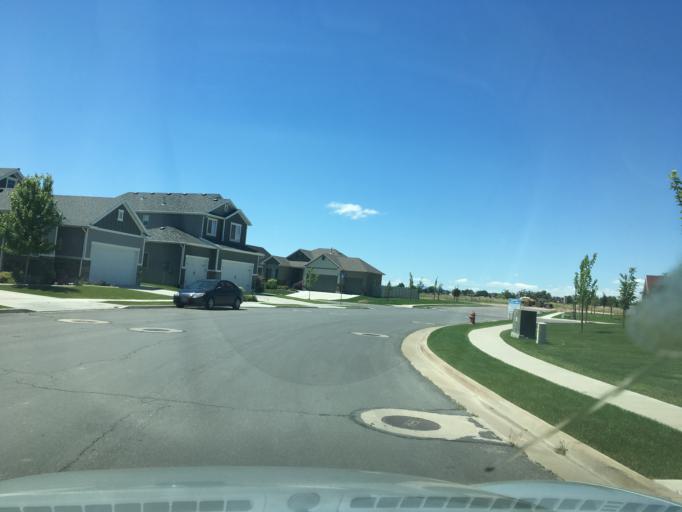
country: US
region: Utah
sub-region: Davis County
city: Layton
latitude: 41.0534
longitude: -112.0117
